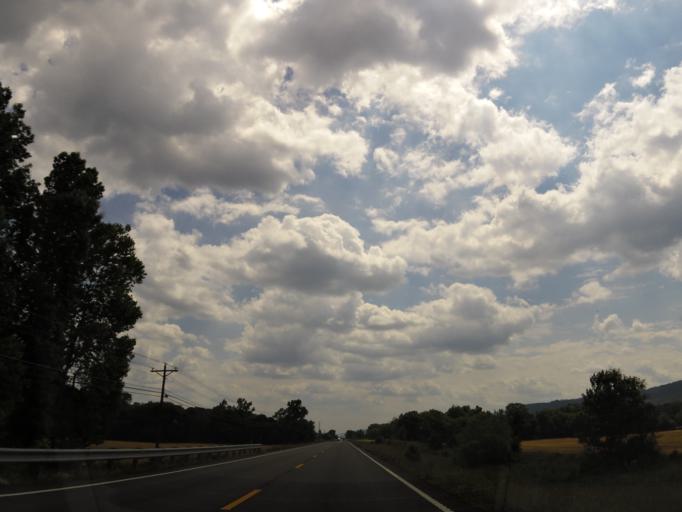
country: US
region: Tennessee
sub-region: Sequatchie County
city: Dunlap
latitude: 35.4923
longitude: -85.3004
